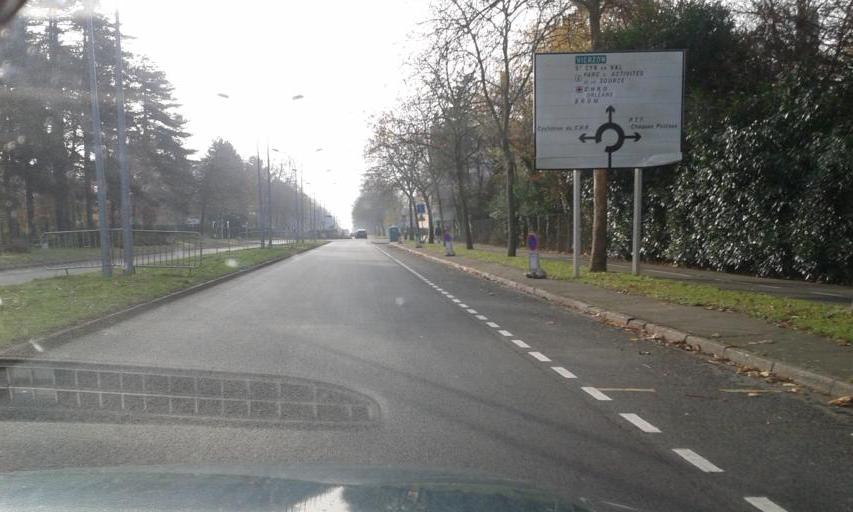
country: FR
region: Centre
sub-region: Departement du Loiret
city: Saint-Cyr-en-Val
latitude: 47.8351
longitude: 1.9409
